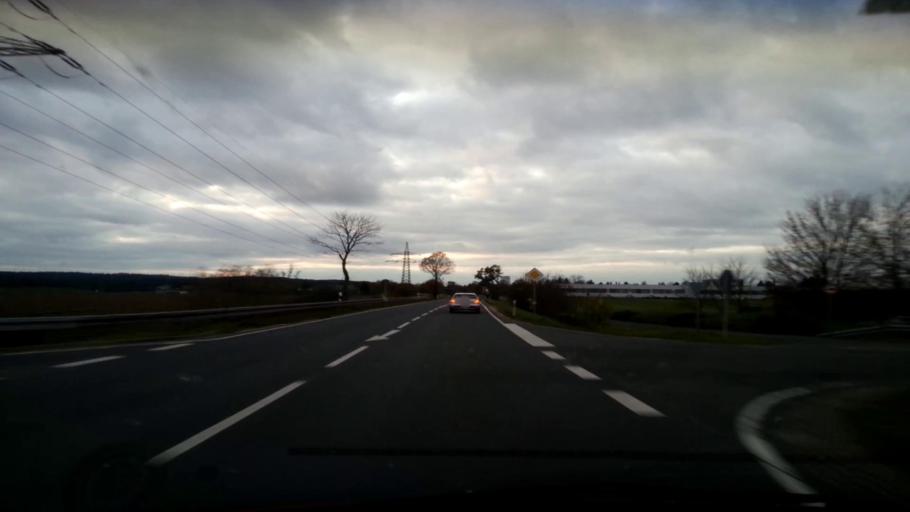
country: DE
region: Bavaria
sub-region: Upper Franconia
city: Sonnefeld
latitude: 50.2129
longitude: 11.0856
